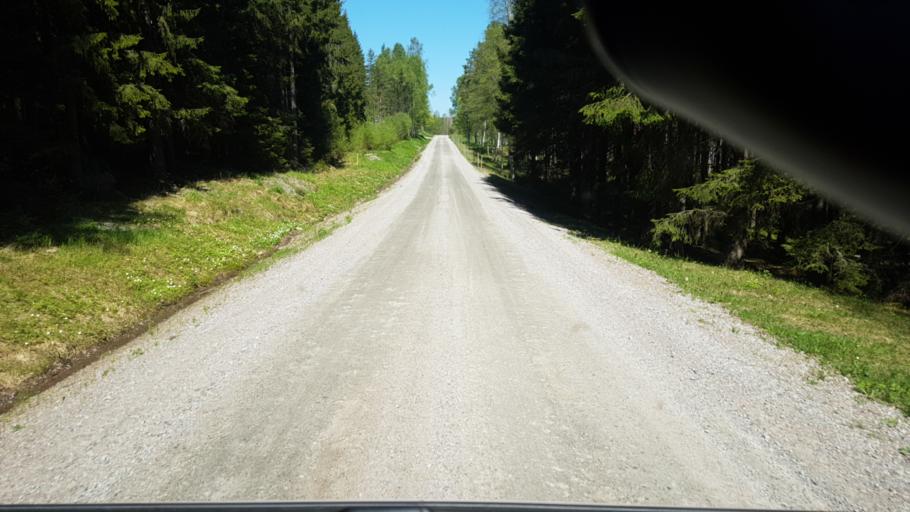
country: SE
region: Vaermland
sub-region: Arvika Kommun
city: Arvika
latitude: 59.8271
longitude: 12.7467
